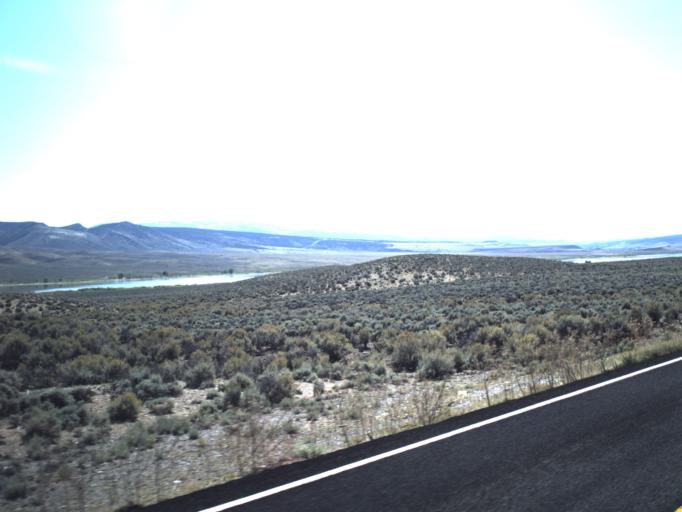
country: US
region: Utah
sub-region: Piute County
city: Junction
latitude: 38.2167
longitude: -112.0013
